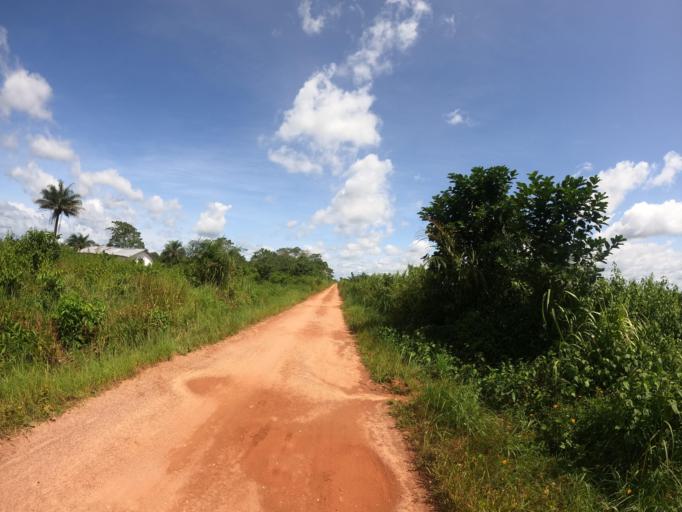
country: SL
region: Northern Province
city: Masingbi
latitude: 8.8305
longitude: -11.9910
